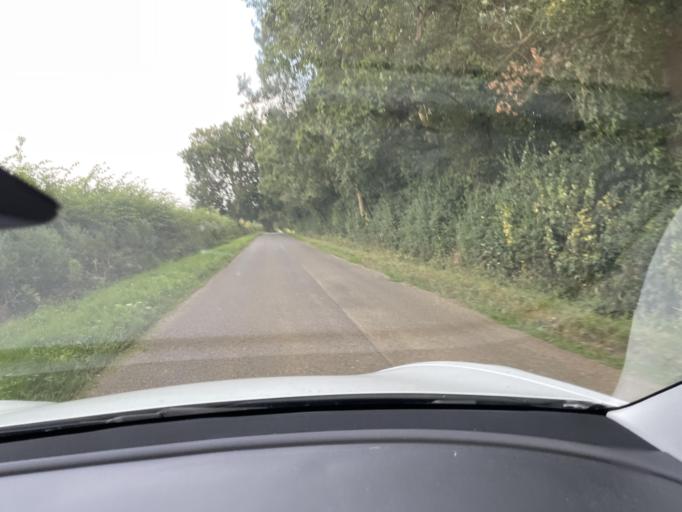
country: GB
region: England
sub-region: Leicestershire
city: Market Harborough
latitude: 52.4047
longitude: -1.0068
